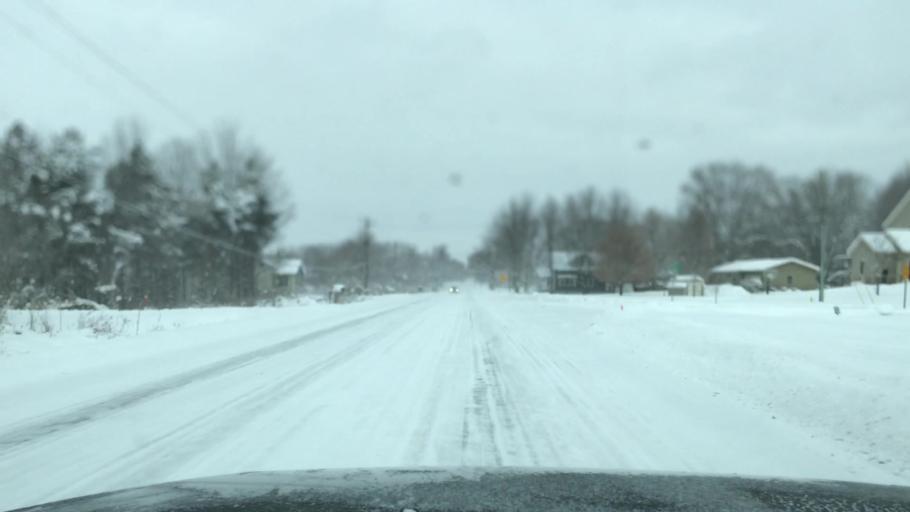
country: US
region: Michigan
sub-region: Ottawa County
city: Hudsonville
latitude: 42.8192
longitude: -85.8422
